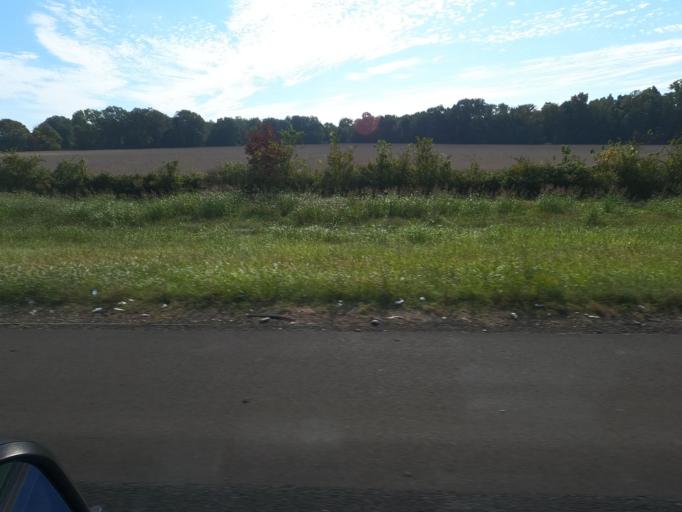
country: US
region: Tennessee
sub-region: Fayette County
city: Hickory Withe
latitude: 35.3139
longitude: -89.5794
